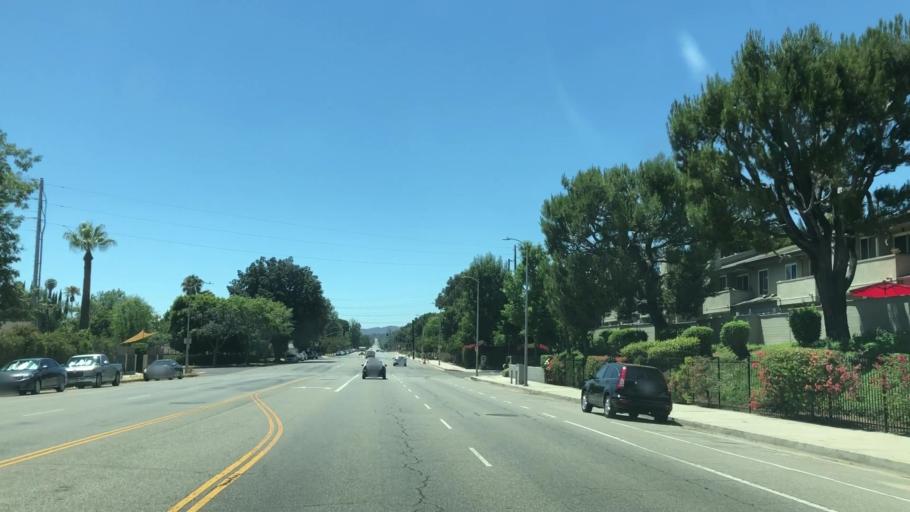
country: US
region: California
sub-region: Los Angeles County
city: San Fernando
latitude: 34.2791
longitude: -118.4731
